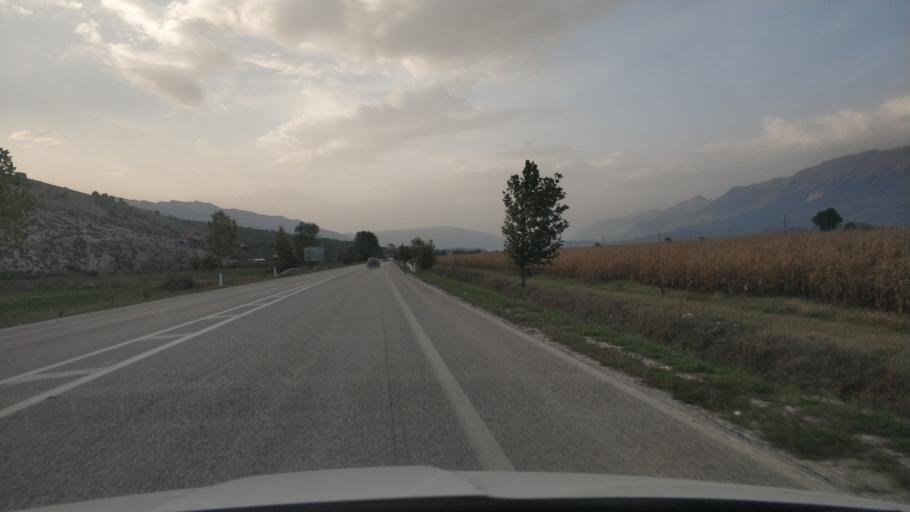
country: AL
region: Gjirokaster
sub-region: Rrethi i Gjirokastres
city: Libohove
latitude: 39.9867
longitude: 20.2235
